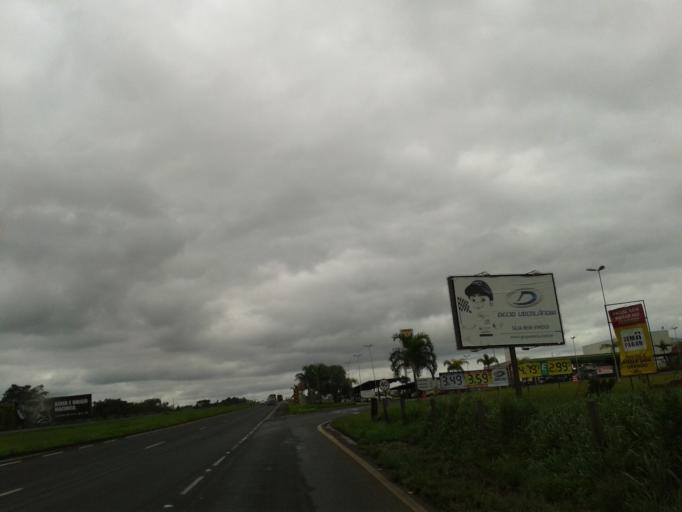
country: BR
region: Minas Gerais
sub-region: Uberlandia
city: Uberlandia
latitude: -19.0132
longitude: -48.2078
